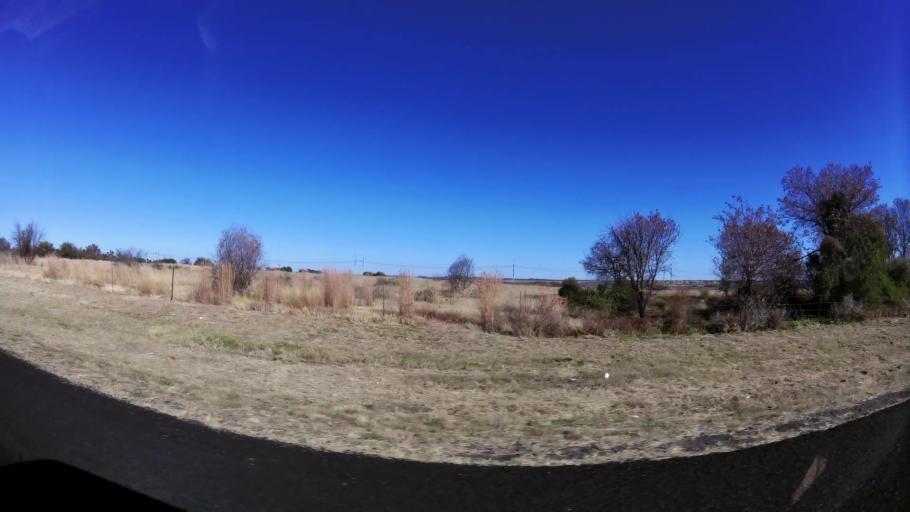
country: ZA
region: Northern Cape
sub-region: Frances Baard District Municipality
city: Kimberley
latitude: -28.6824
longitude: 24.7779
